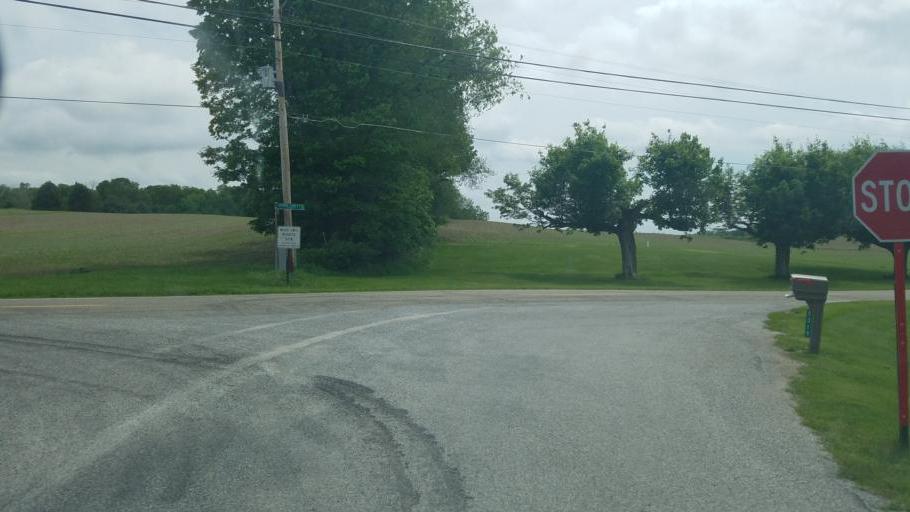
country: US
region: Ohio
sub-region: Licking County
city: Granville
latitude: 40.1333
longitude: -82.5605
